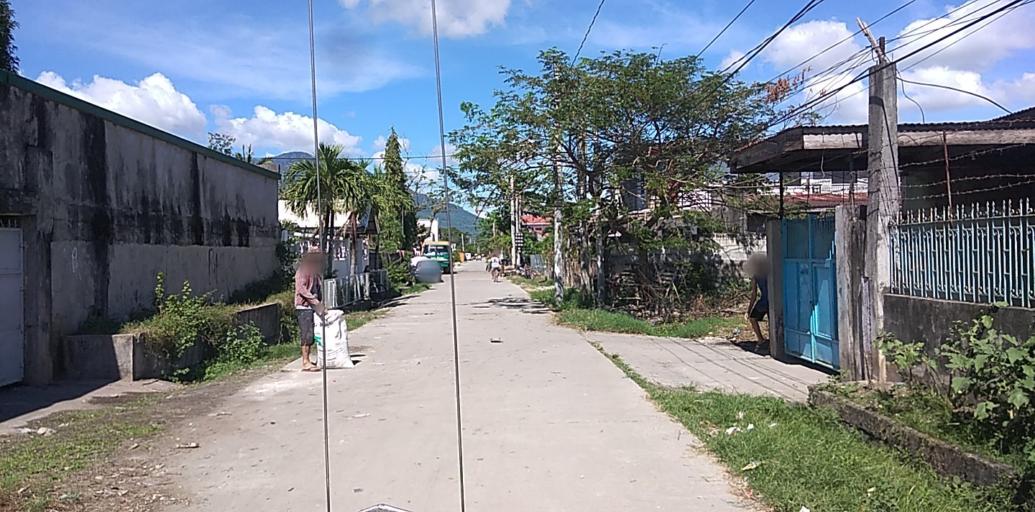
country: PH
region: Central Luzon
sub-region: Province of Pampanga
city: Arayat
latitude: 15.1342
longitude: 120.7754
